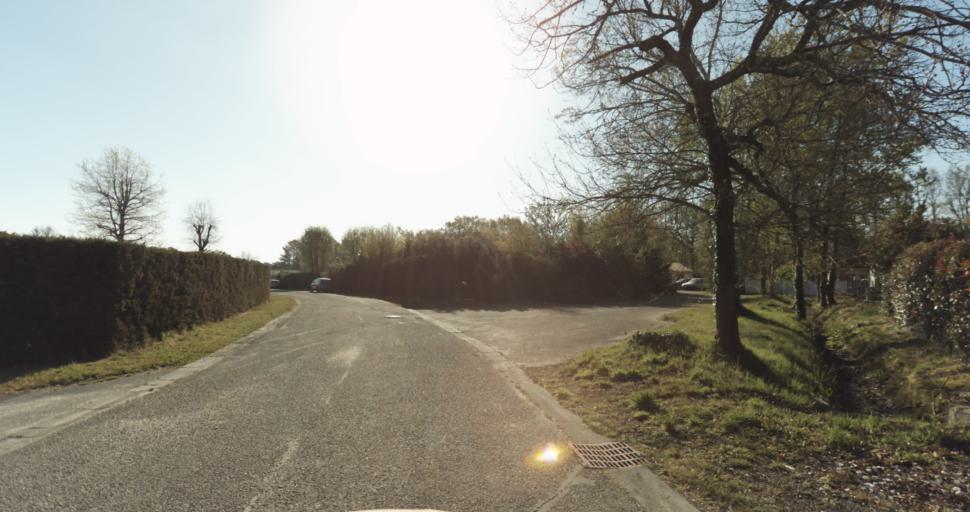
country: FR
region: Aquitaine
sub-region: Departement de la Gironde
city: Martignas-sur-Jalle
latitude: 44.8001
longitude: -0.8364
